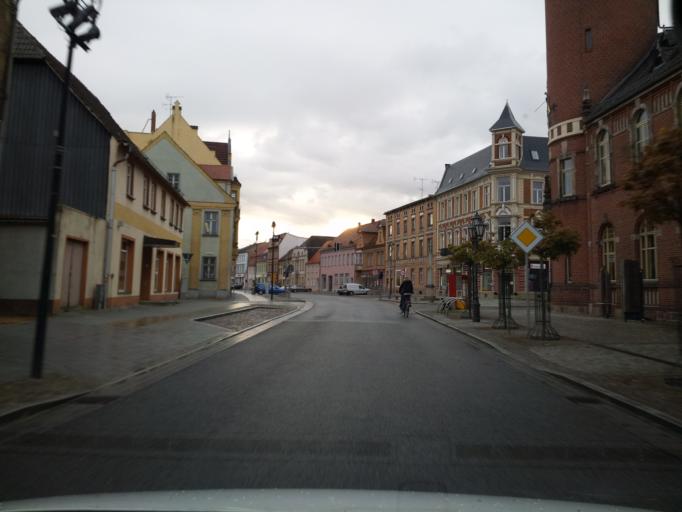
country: DE
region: Brandenburg
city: Dahme
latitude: 51.8694
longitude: 13.4287
